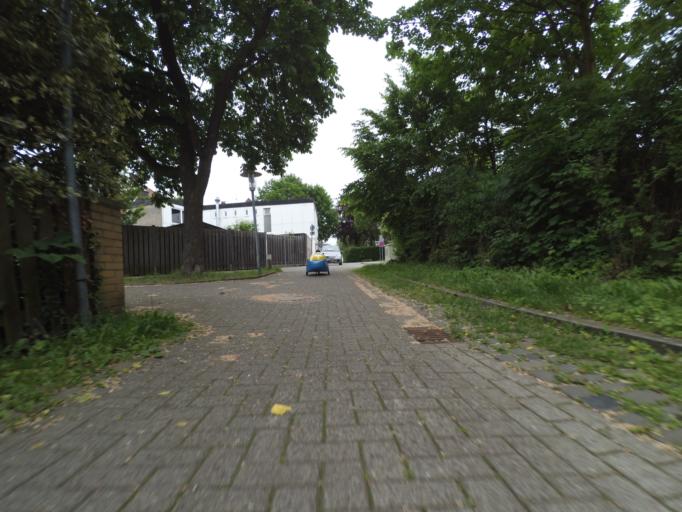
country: DE
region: Lower Saxony
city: Burgdorf
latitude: 52.4460
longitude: 10.0107
